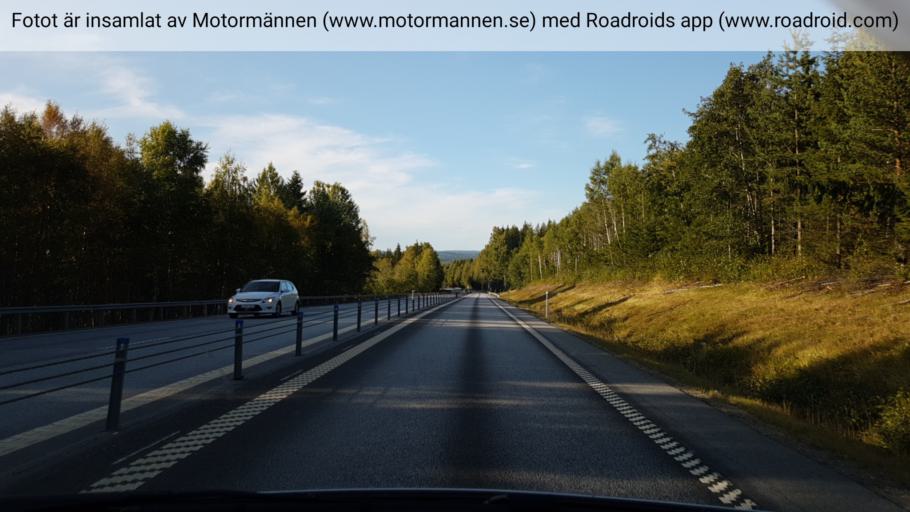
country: SE
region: Vaesterbotten
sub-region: Vannas Kommun
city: Vannasby
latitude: 63.9065
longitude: 19.8910
